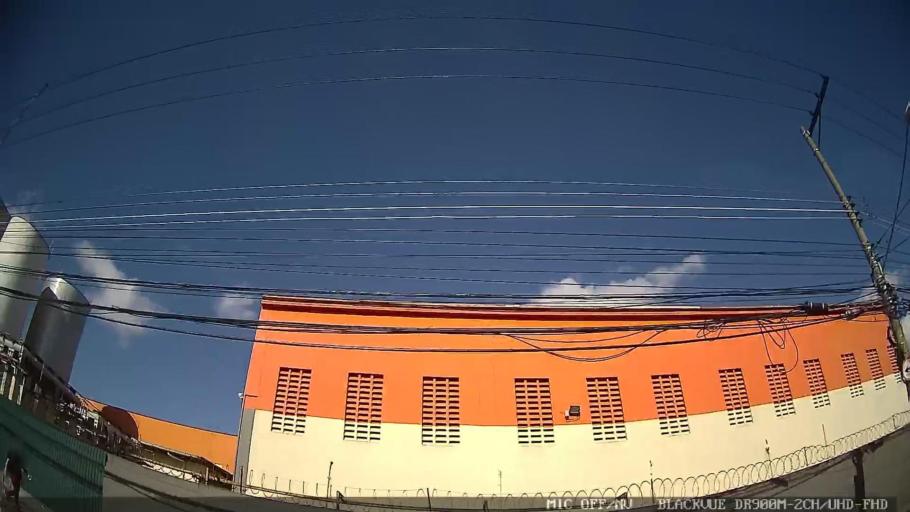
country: BR
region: Sao Paulo
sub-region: Sao Paulo
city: Sao Paulo
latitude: -23.5819
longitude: -46.6011
